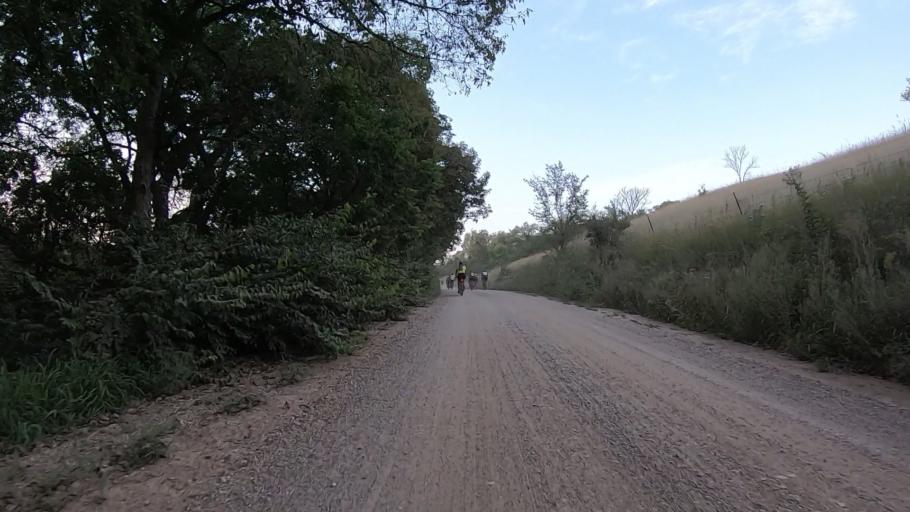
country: US
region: Kansas
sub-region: Marshall County
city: Marysville
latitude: 39.8359
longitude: -96.6655
